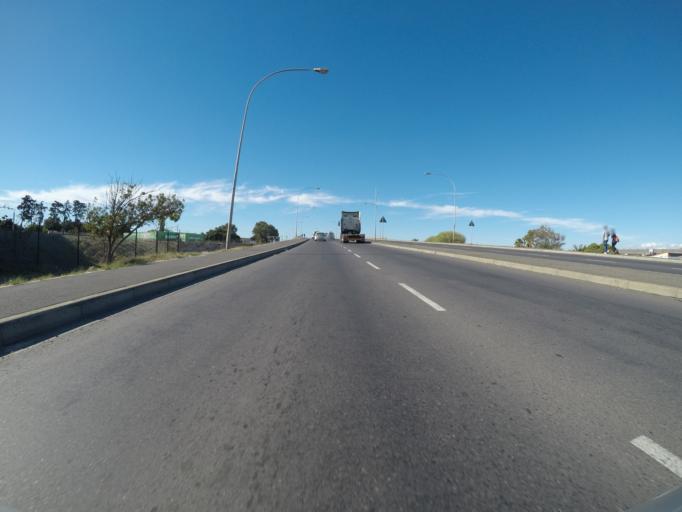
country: ZA
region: Western Cape
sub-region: City of Cape Town
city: Kraaifontein
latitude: -33.8948
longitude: 18.6723
